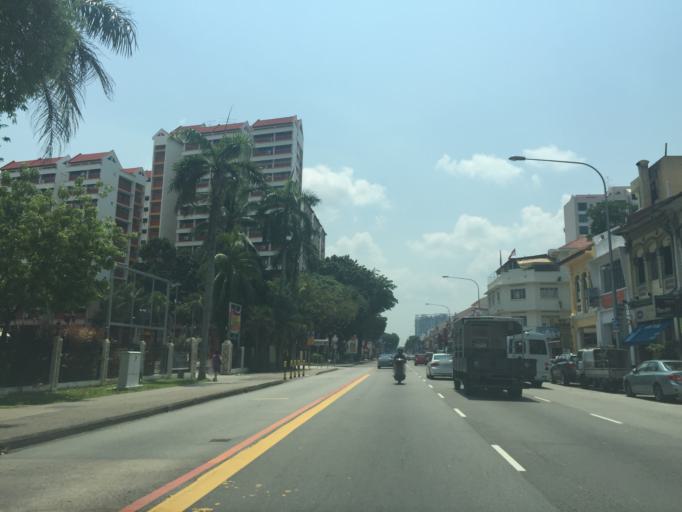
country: SG
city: Singapore
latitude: 1.3130
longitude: 103.8563
